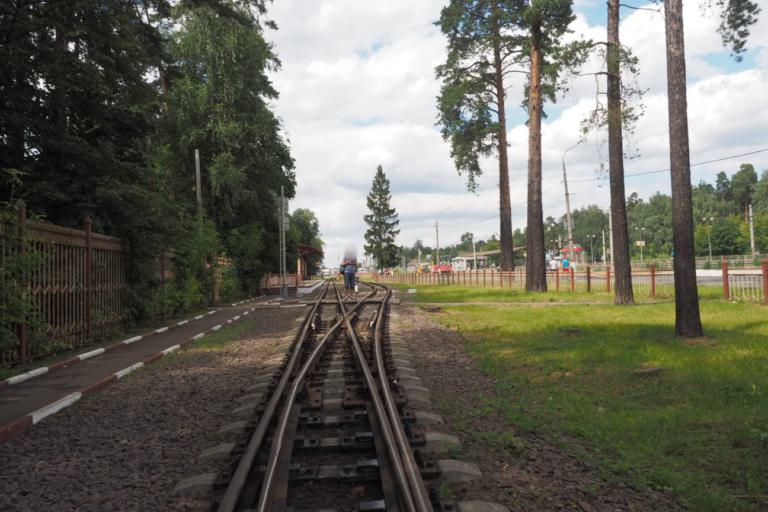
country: RU
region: Moskovskaya
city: Zhukovskiy
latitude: 55.6002
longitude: 38.1384
